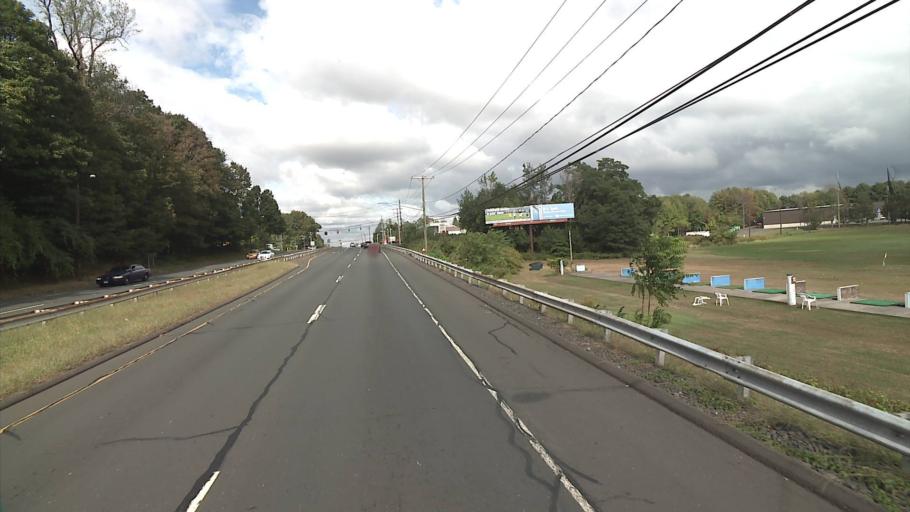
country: US
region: Connecticut
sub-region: Hartford County
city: Kensington
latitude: 41.5963
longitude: -72.7556
